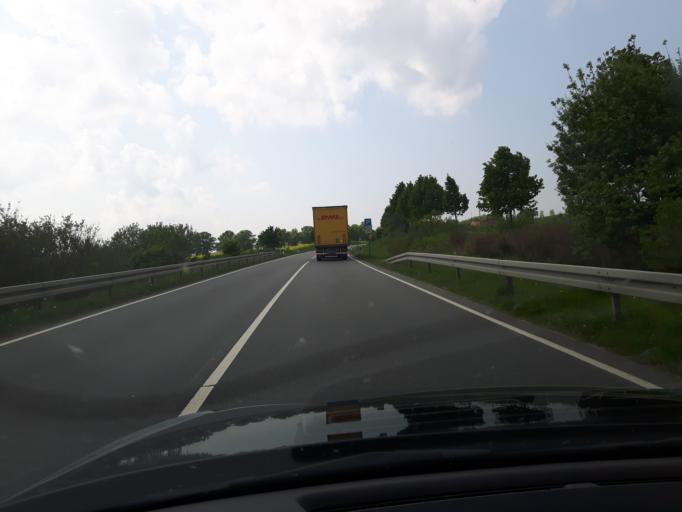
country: DE
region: Mecklenburg-Vorpommern
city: Selmsdorf
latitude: 53.8640
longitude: 10.9117
